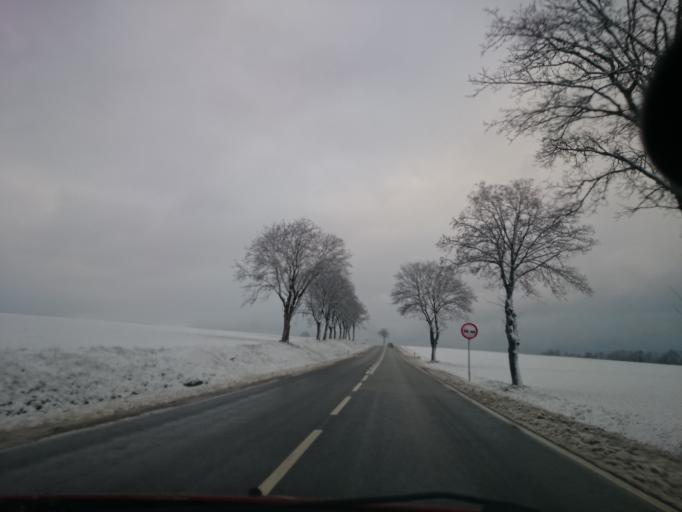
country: PL
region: Lower Silesian Voivodeship
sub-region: Powiat klodzki
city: Bystrzyca Klodzka
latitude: 50.3319
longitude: 16.6630
